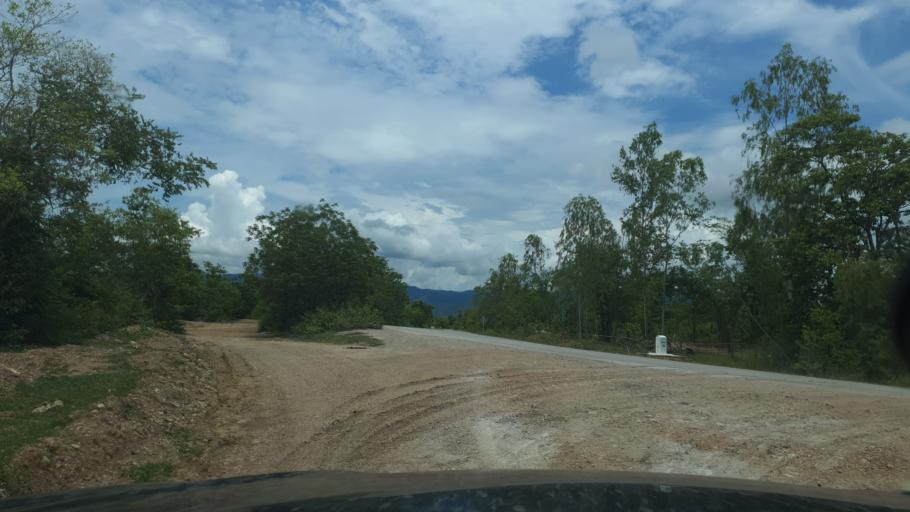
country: TH
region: Lampang
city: Sop Prap
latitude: 17.9340
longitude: 99.3653
